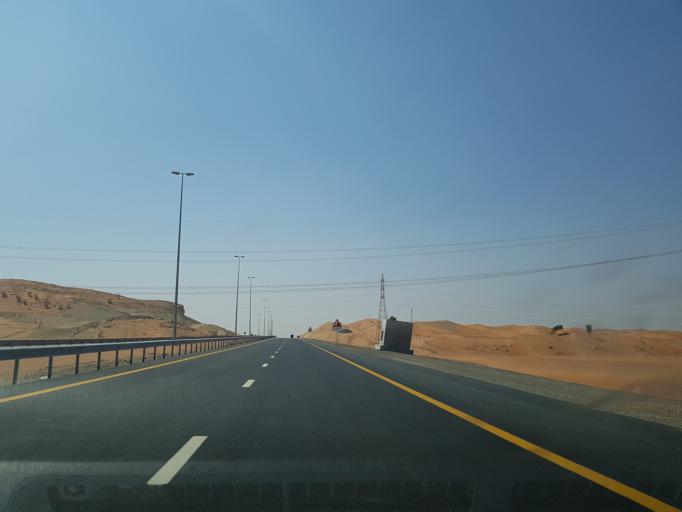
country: AE
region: Ash Shariqah
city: Adh Dhayd
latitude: 25.2466
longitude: 55.8465
